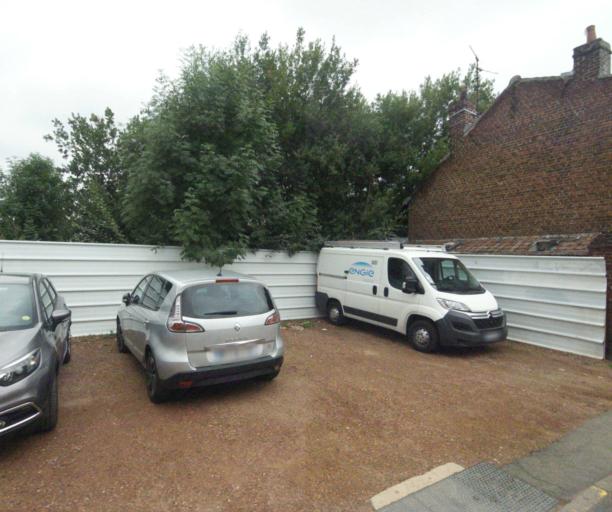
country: FR
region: Nord-Pas-de-Calais
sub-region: Departement du Nord
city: Lezennes
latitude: 50.6137
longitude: 3.1144
